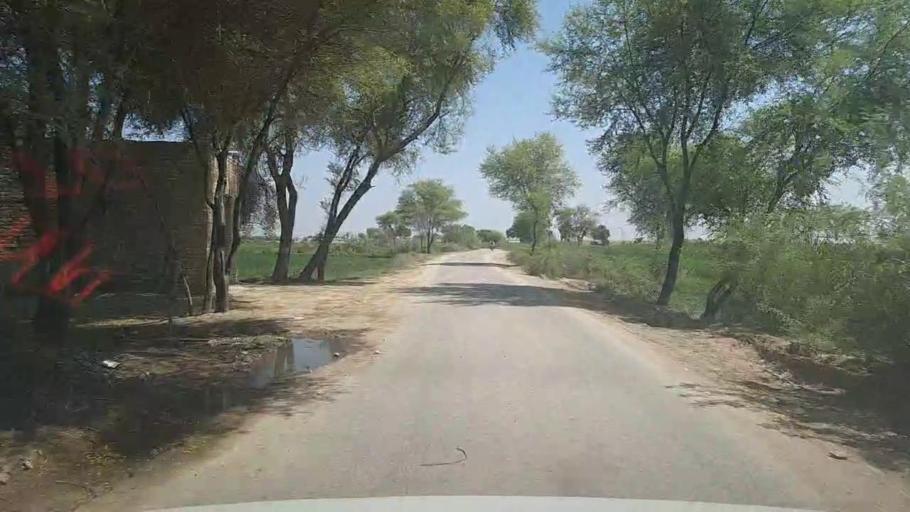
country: PK
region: Sindh
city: Kashmor
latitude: 28.2834
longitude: 69.4388
